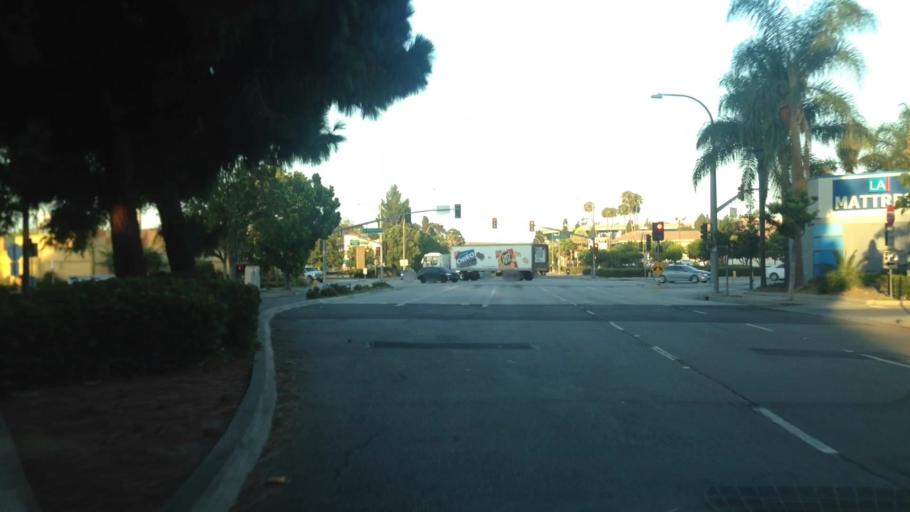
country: US
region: California
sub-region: Los Angeles County
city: Ladera Heights
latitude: 33.9908
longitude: -118.3944
